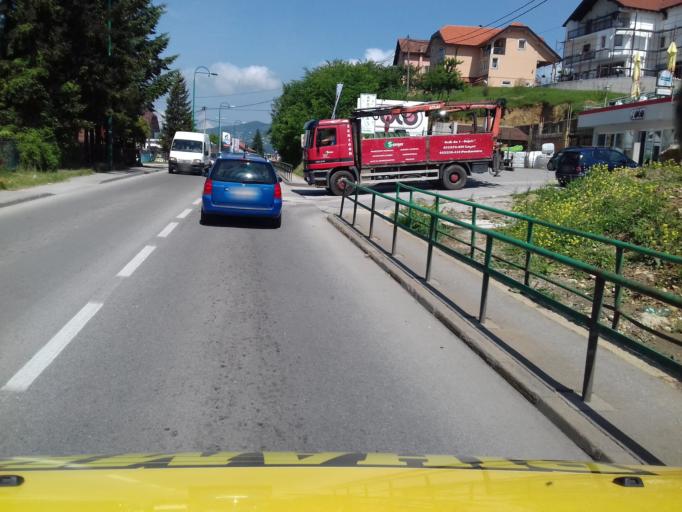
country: BA
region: Federation of Bosnia and Herzegovina
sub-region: Kanton Sarajevo
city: Sarajevo
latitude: 43.8561
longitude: 18.3243
